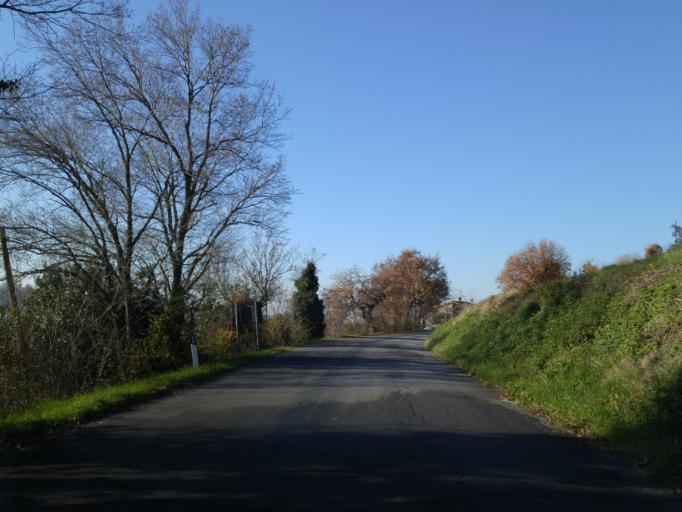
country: IT
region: The Marches
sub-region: Provincia di Pesaro e Urbino
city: Isola del Piano
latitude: 43.7672
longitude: 12.8006
